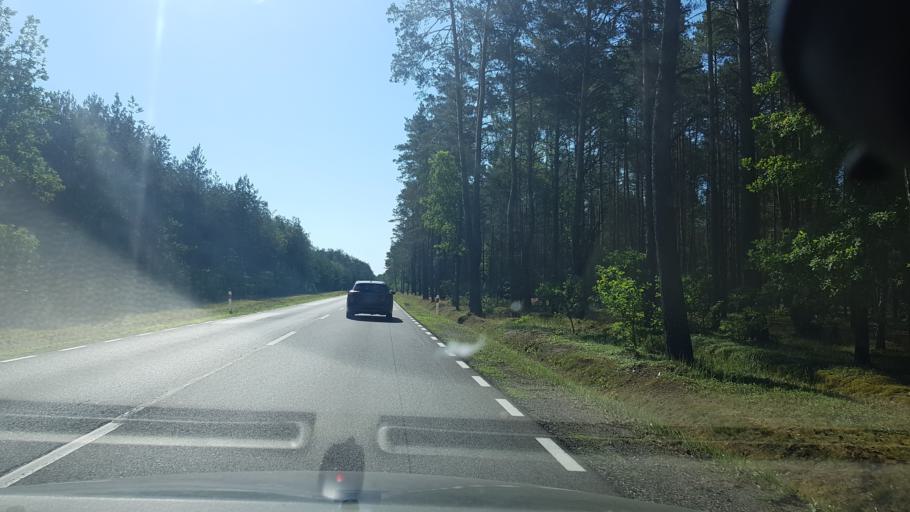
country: PL
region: Masovian Voivodeship
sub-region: Powiat wyszkowski
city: Branszczyk
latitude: 52.5613
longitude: 21.5715
